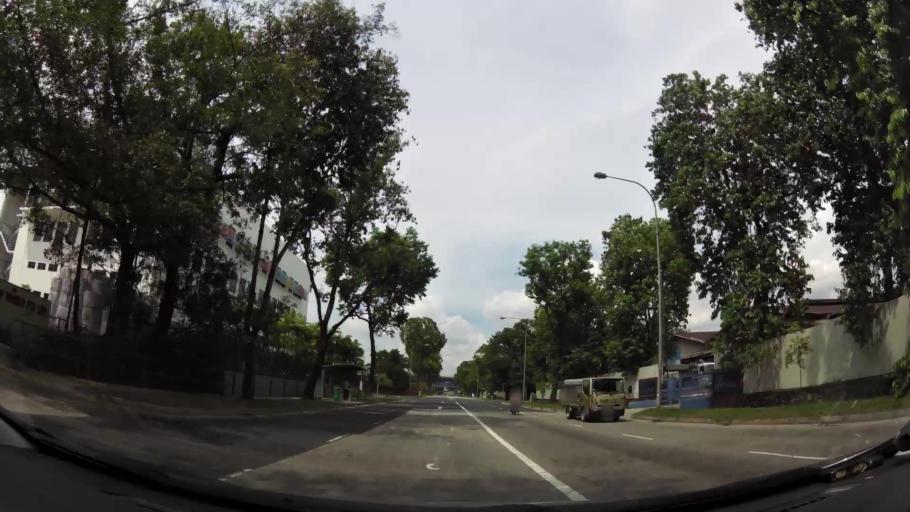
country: MY
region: Johor
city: Johor Bahru
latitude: 1.4190
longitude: 103.7508
